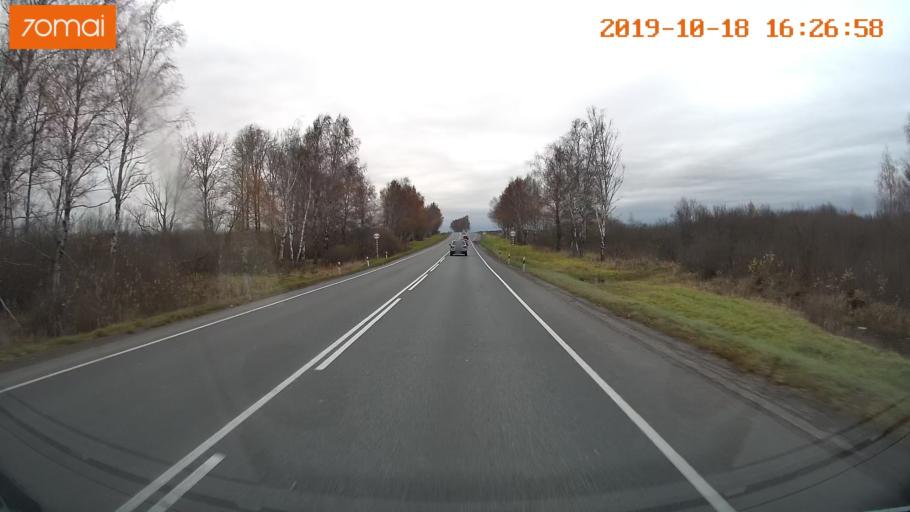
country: RU
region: Vladimir
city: Bogolyubovo
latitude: 56.2958
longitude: 40.4694
